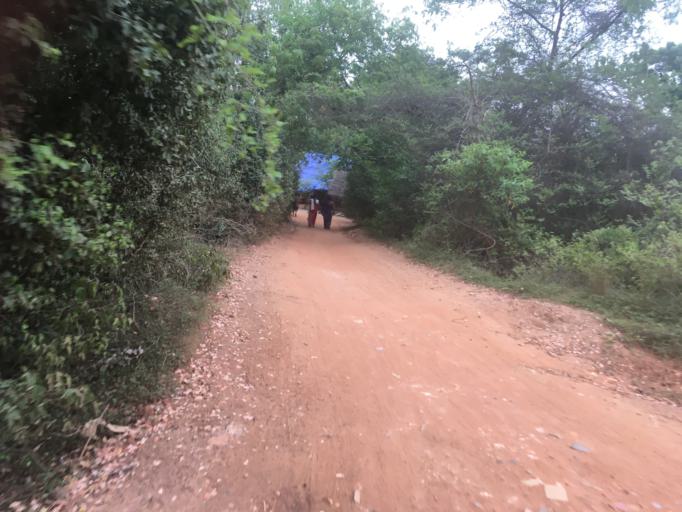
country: IN
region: Tamil Nadu
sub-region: Villupuram
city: Auroville
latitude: 12.0133
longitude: 79.8053
